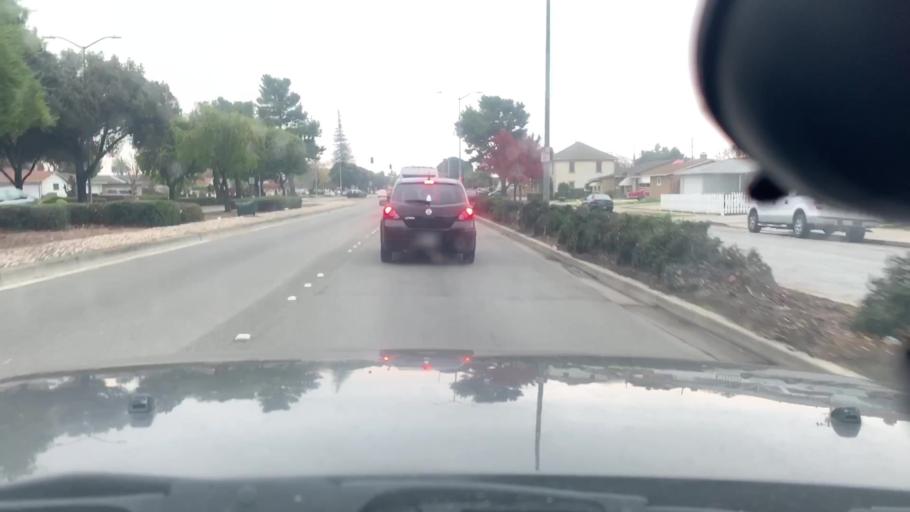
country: US
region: California
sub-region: Alameda County
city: Fremont
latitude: 37.5345
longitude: -121.9782
